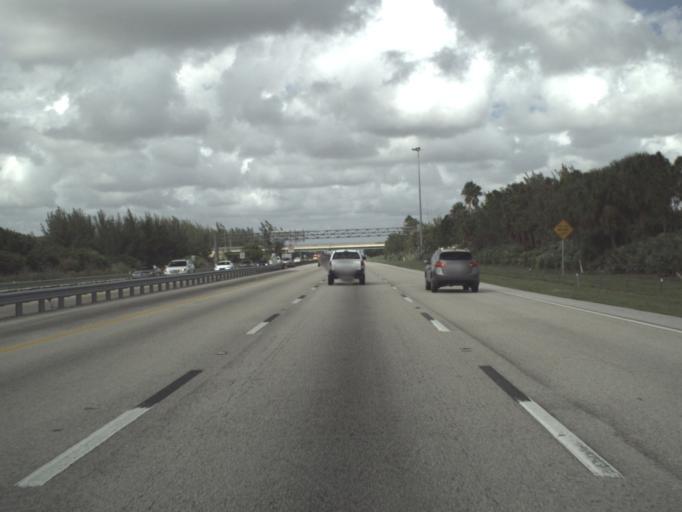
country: US
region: Florida
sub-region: Palm Beach County
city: Greenacres City
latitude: 26.5671
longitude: -80.1730
